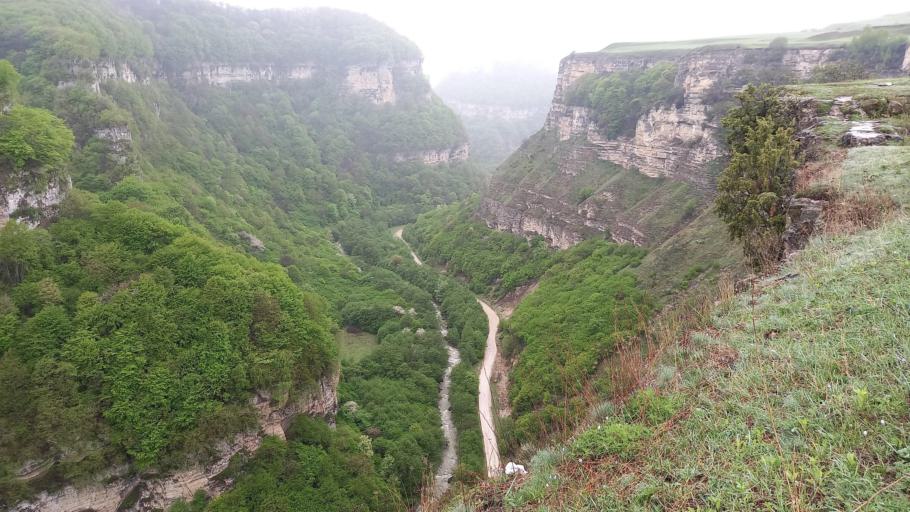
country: RU
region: Kabardino-Balkariya
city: Gundelen
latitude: 43.5947
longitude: 43.1355
